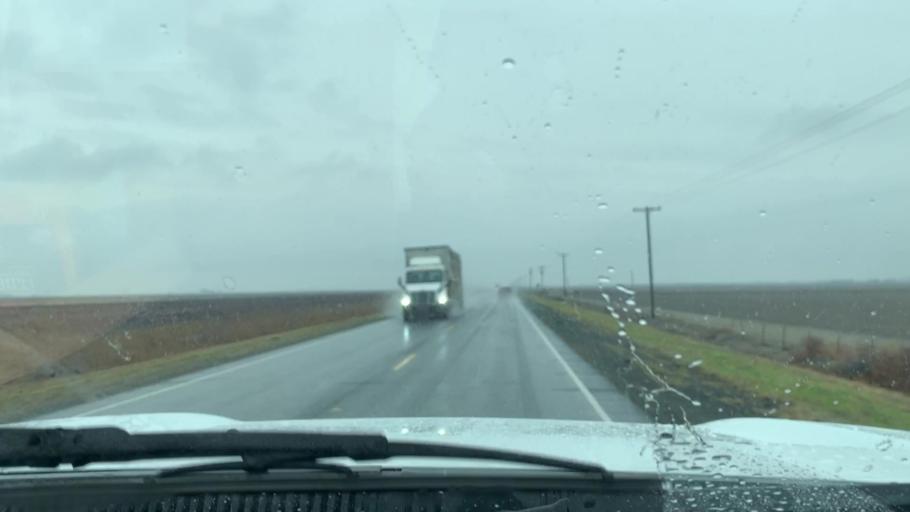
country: US
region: California
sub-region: Tulare County
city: Alpaugh
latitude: 35.9217
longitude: -119.4274
